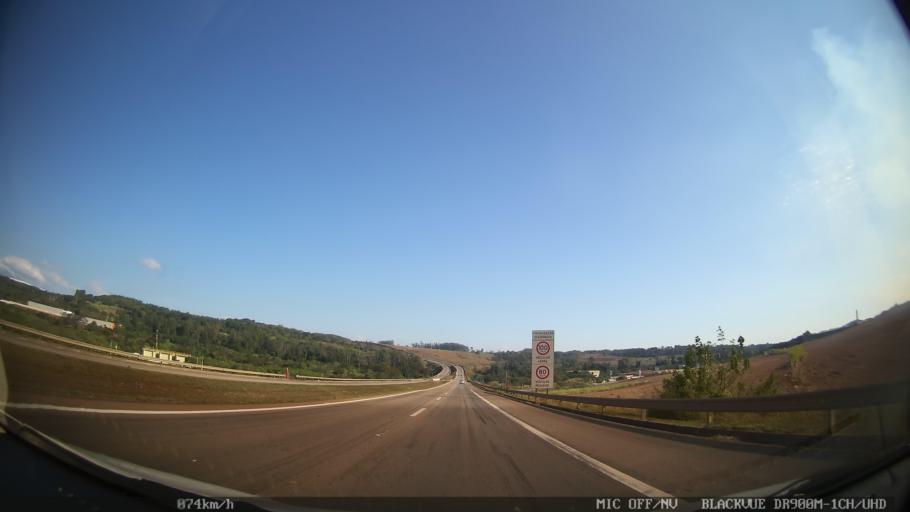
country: BR
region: Sao Paulo
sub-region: Piracicaba
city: Piracicaba
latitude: -22.6973
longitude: -47.6058
